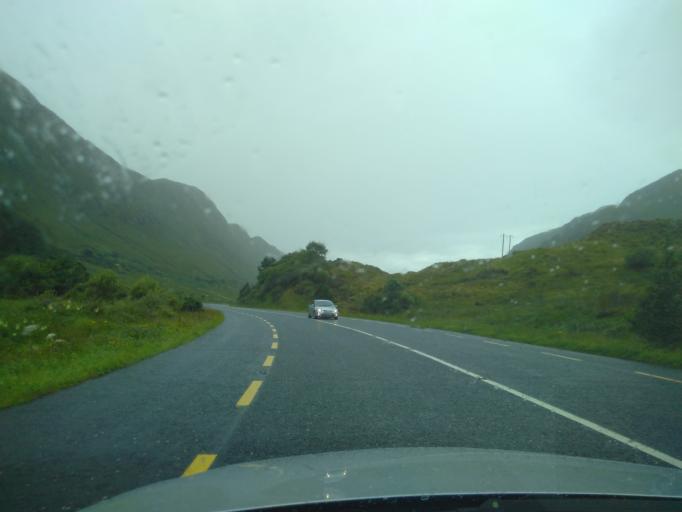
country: IE
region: Ulster
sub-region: County Donegal
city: Ballybofey
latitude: 54.7271
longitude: -7.9438
